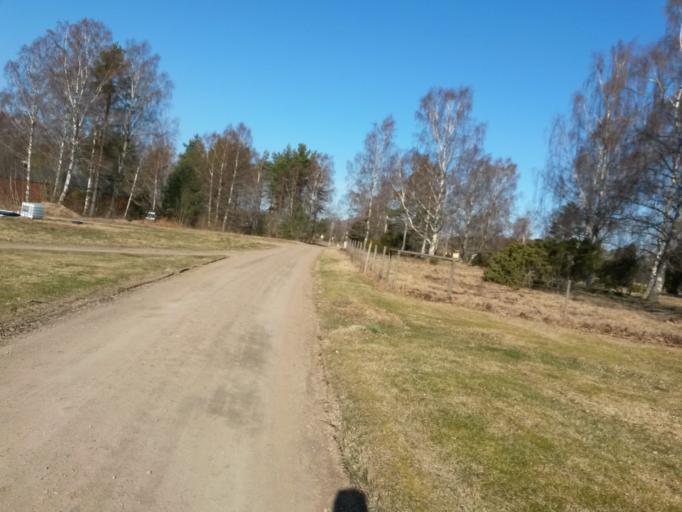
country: SE
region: Vaestra Goetaland
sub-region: Vargarda Kommun
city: Vargarda
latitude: 58.0260
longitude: 12.8289
